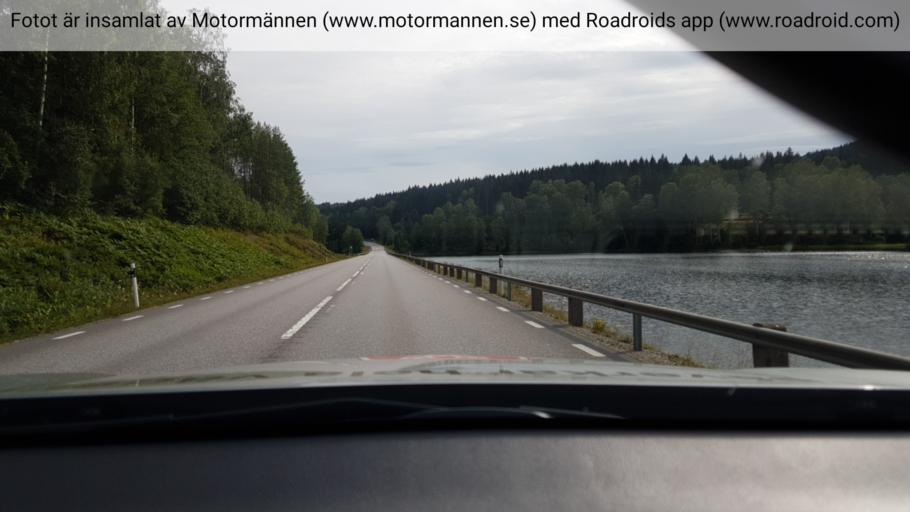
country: SE
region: Vaestra Goetaland
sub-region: Bengtsfors Kommun
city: Dals Langed
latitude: 59.0552
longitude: 12.4400
